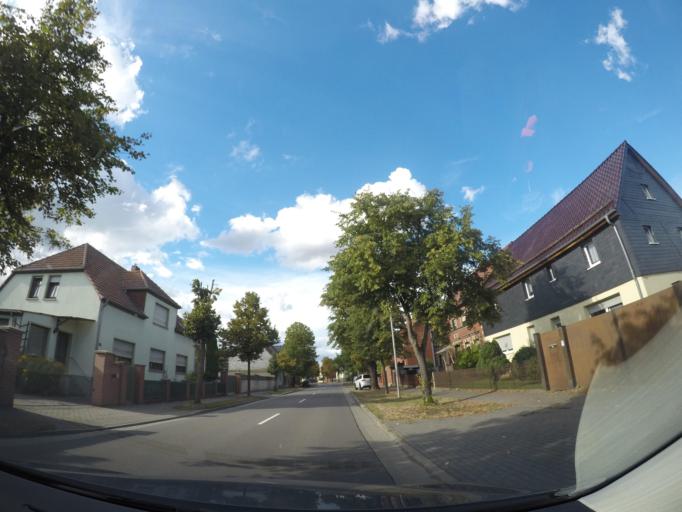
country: DE
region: Saxony-Anhalt
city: Bulstringen
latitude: 52.3192
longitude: 11.3481
